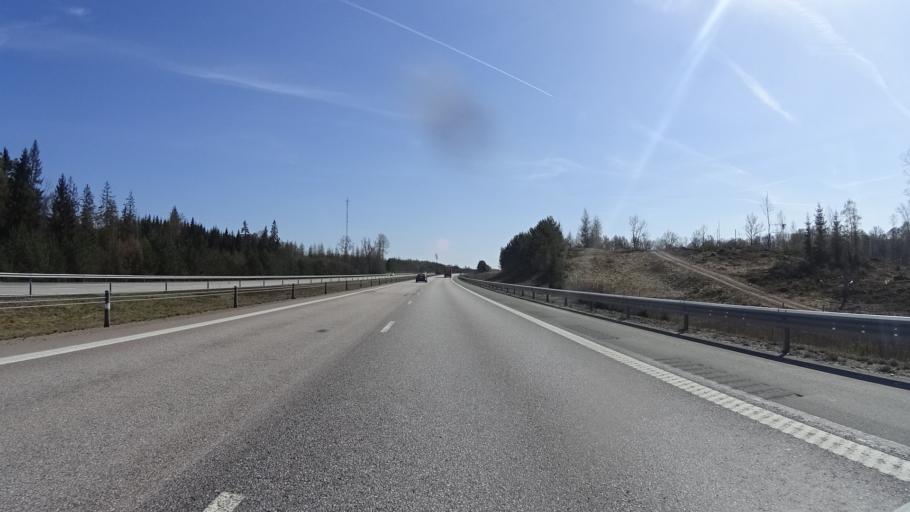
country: SE
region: Joenkoeping
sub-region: Varnamo Kommun
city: Varnamo
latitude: 57.0969
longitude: 14.0654
